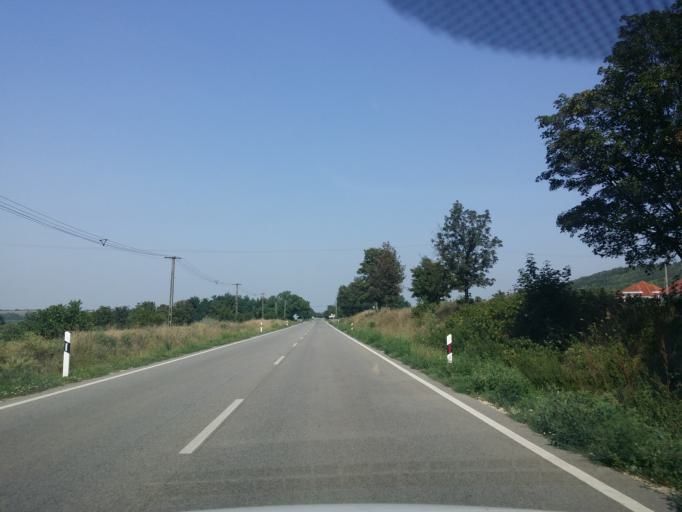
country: HU
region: Tolna
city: Simontornya
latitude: 46.7411
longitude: 18.5185
